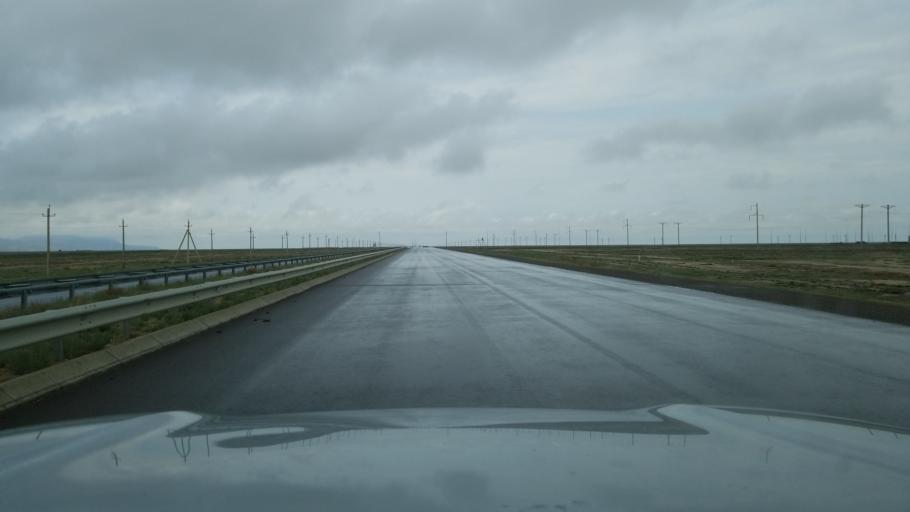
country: TM
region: Balkan
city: Gazanjyk
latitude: 39.1456
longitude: 55.8643
